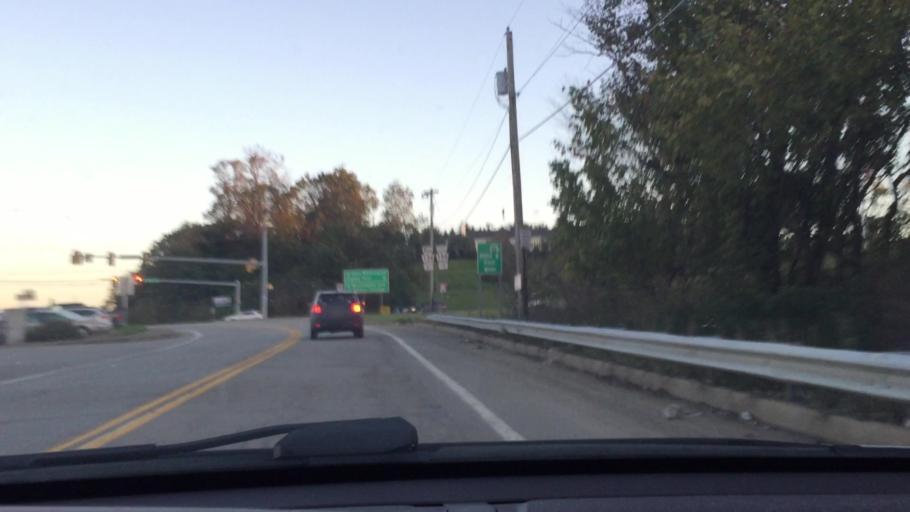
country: US
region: Pennsylvania
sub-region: Washington County
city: East Washington
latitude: 40.1797
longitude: -80.2220
